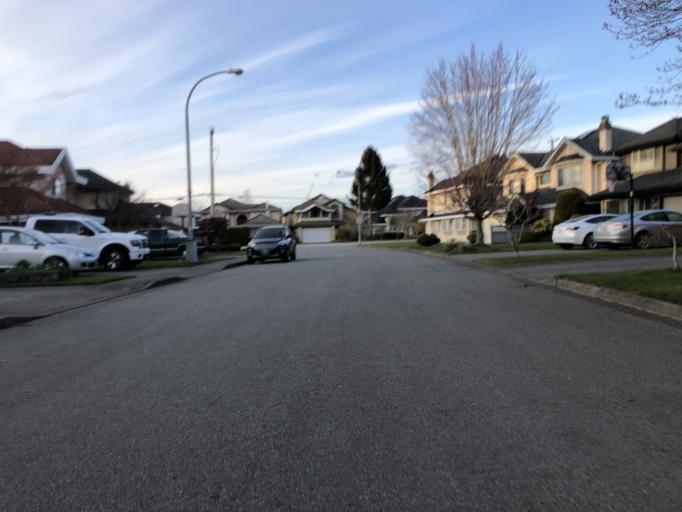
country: CA
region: British Columbia
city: Richmond
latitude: 49.1511
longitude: -123.1239
